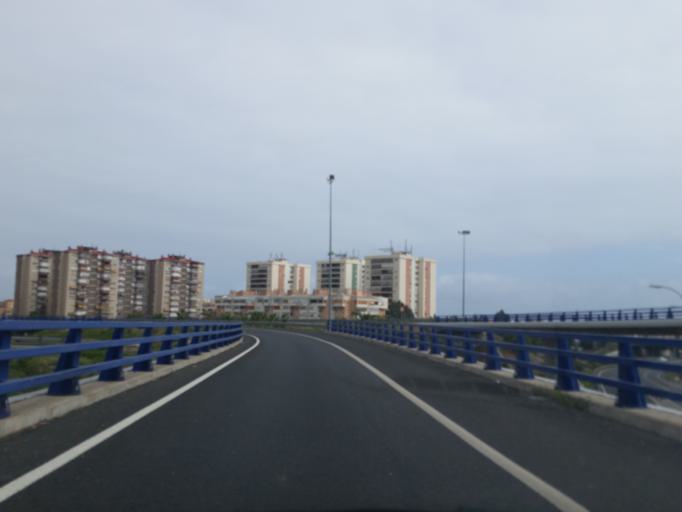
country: ES
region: Andalusia
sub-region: Provincia de Malaga
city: Malaga
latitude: 36.7118
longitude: -4.4601
